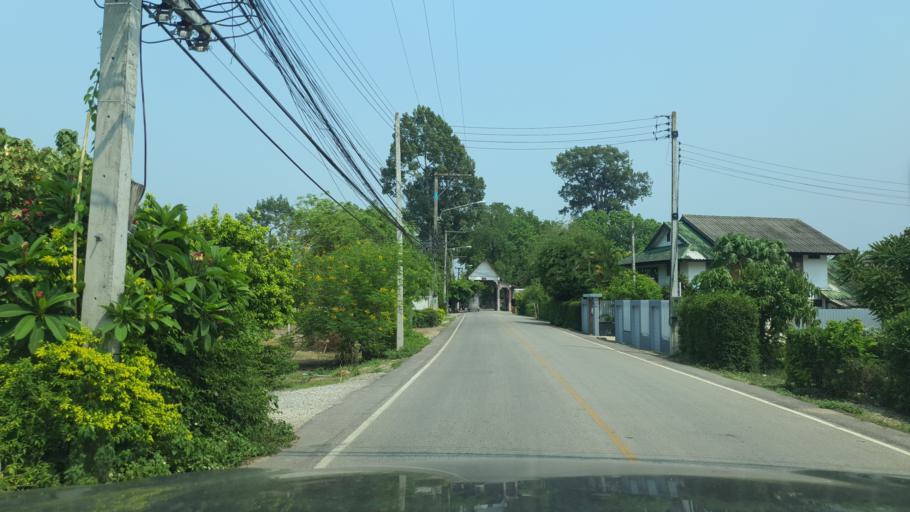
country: TH
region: Chiang Mai
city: Saraphi
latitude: 18.6729
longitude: 98.9841
